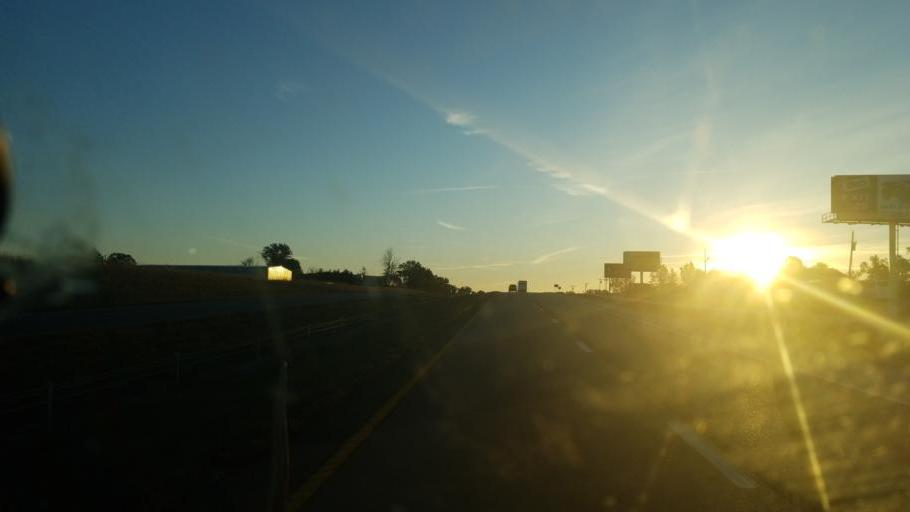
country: US
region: Missouri
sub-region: Boone County
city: Hallsville
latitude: 38.9538
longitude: -92.1410
